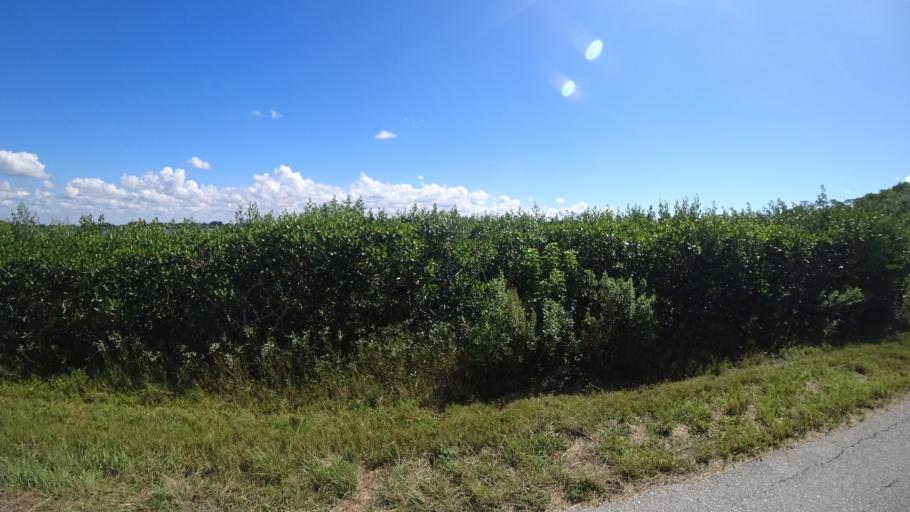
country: US
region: Florida
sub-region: Manatee County
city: Memphis
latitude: 27.5762
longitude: -82.5672
